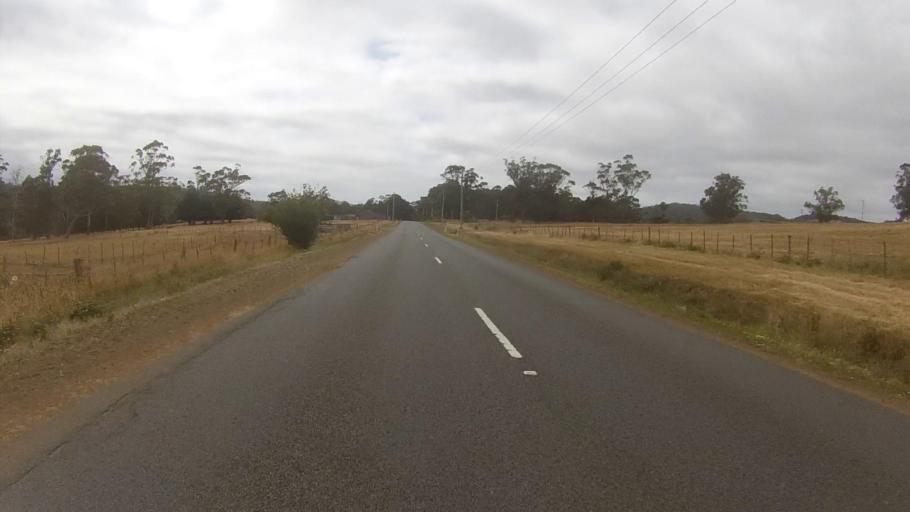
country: AU
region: Tasmania
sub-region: Kingborough
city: Margate
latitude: -42.9925
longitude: 147.2007
